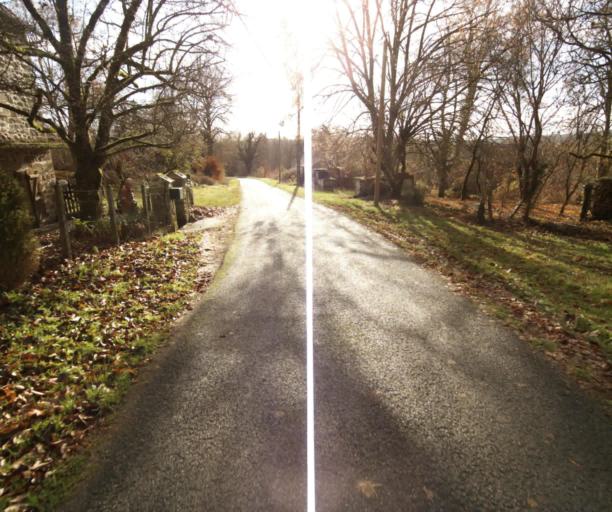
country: FR
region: Limousin
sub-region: Departement de la Correze
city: Sainte-Fereole
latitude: 45.2630
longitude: 1.5950
